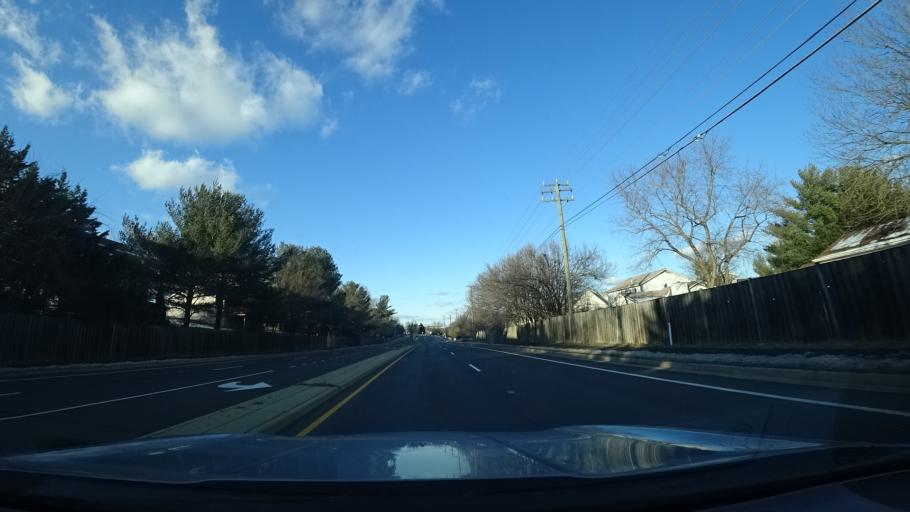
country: US
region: Virginia
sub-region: Fairfax County
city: Herndon
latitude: 38.9967
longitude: -77.3767
